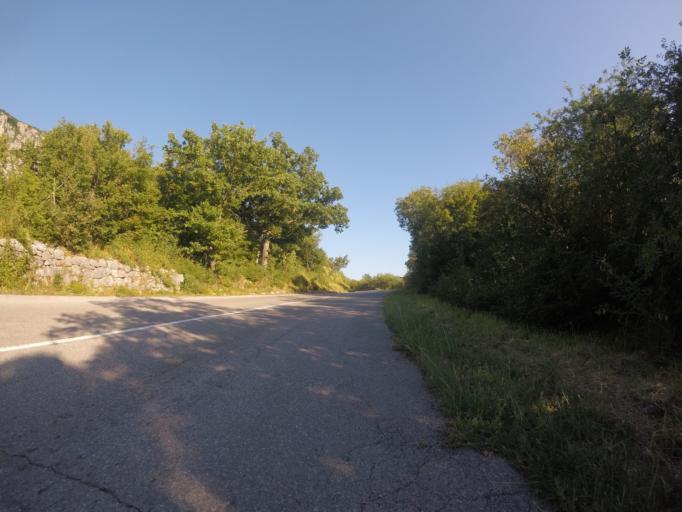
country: HR
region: Primorsko-Goranska
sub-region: Grad Crikvenica
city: Crikvenica
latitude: 45.2126
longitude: 14.7075
